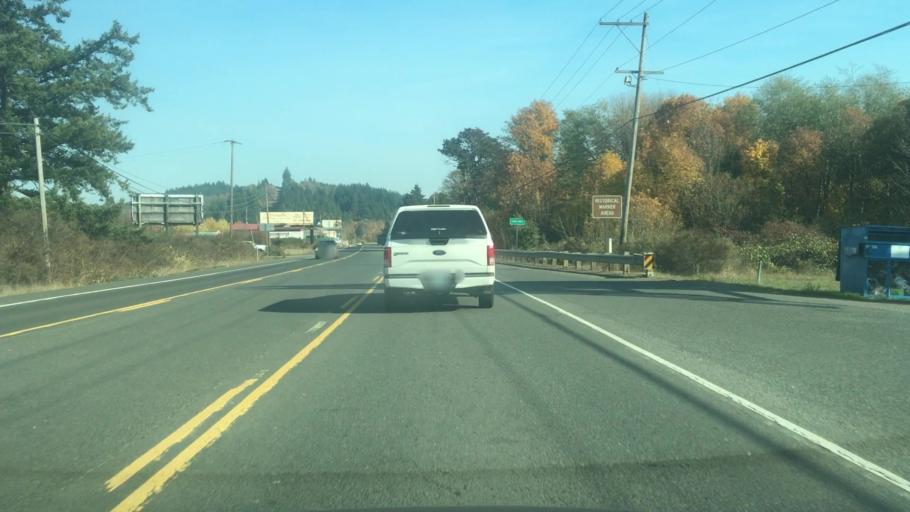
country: US
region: Oregon
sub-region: Polk County
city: Grand Ronde
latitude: 45.0584
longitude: -123.6149
